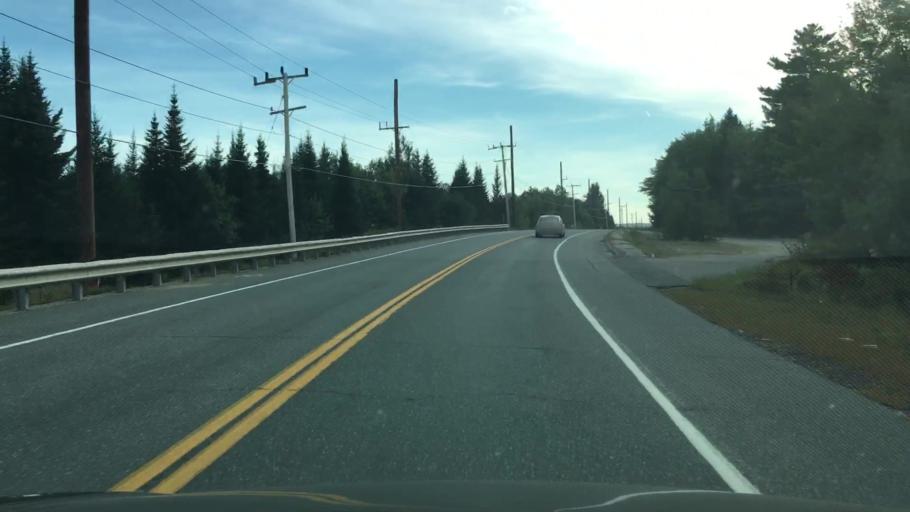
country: US
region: Maine
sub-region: Hancock County
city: Surry
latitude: 44.4608
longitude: -68.5385
